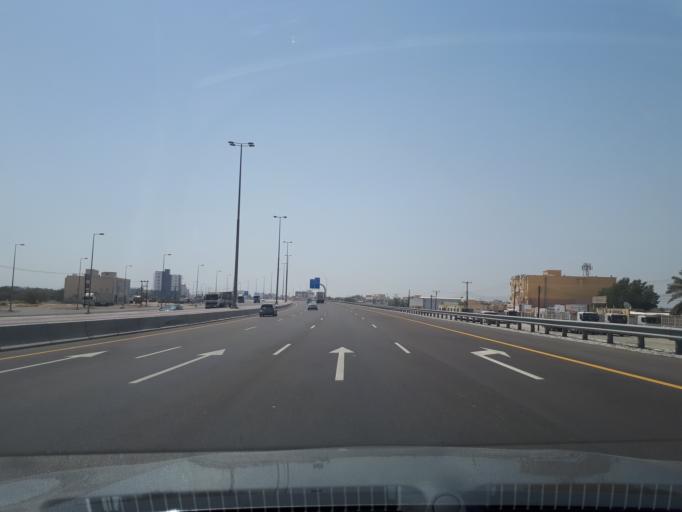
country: OM
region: Al Batinah
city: Al Sohar
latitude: 24.4169
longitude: 56.6278
